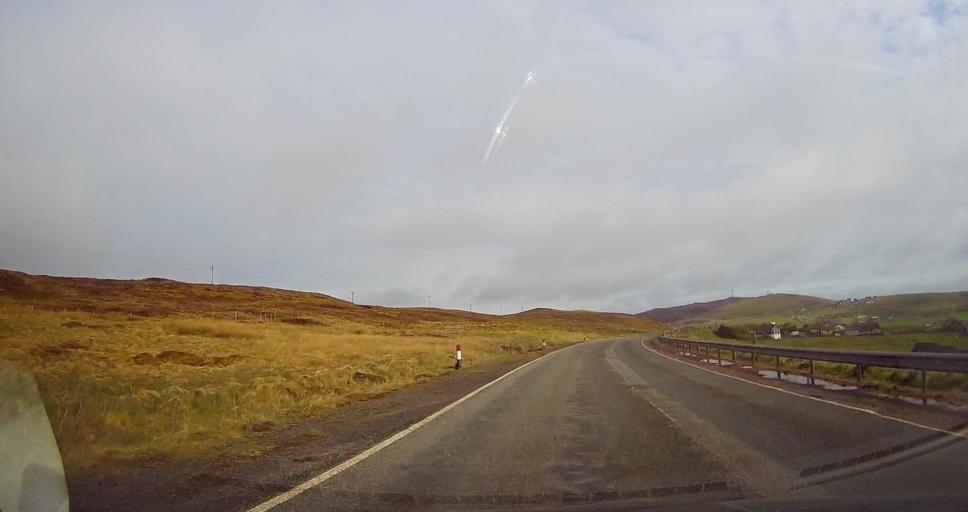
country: GB
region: Scotland
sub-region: Shetland Islands
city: Lerwick
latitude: 60.1245
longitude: -1.2164
